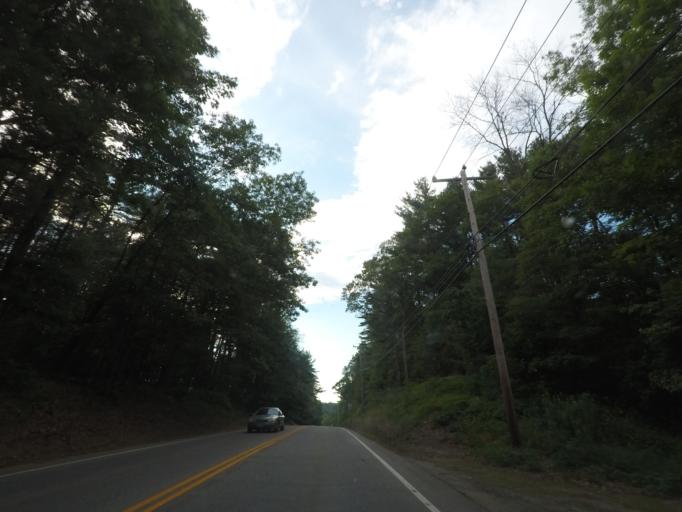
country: US
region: Connecticut
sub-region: Windham County
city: North Grosvenor Dale
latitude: 41.9940
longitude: -71.8992
